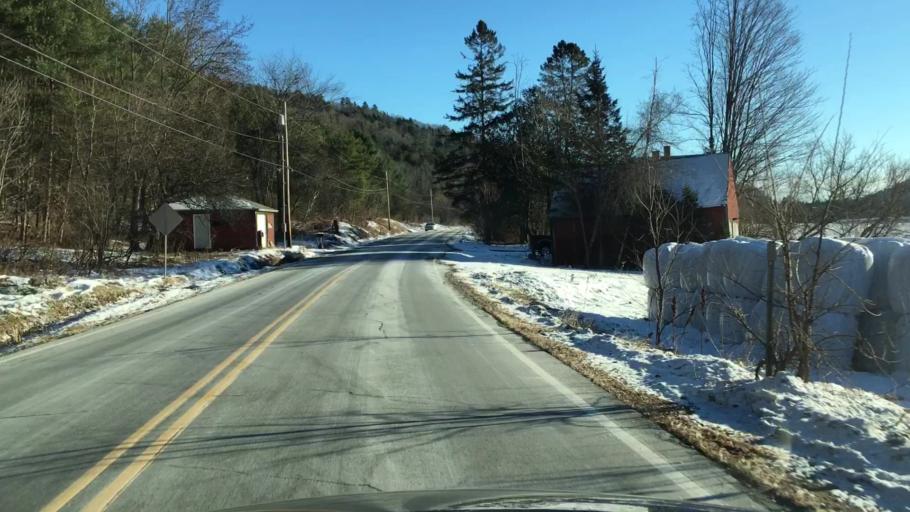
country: US
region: New Hampshire
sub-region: Grafton County
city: Woodsville
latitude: 44.1773
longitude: -72.0488
